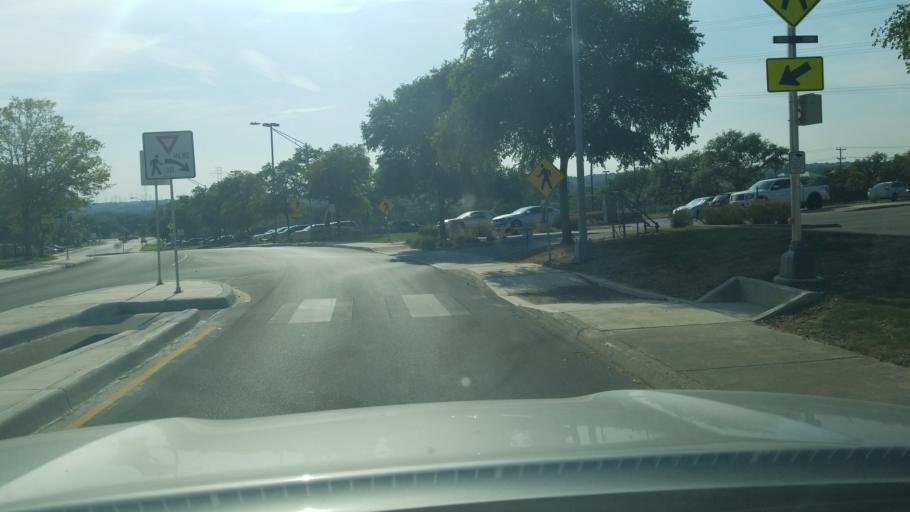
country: US
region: Texas
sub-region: Bexar County
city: Hollywood Park
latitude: 29.6213
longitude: -98.4906
